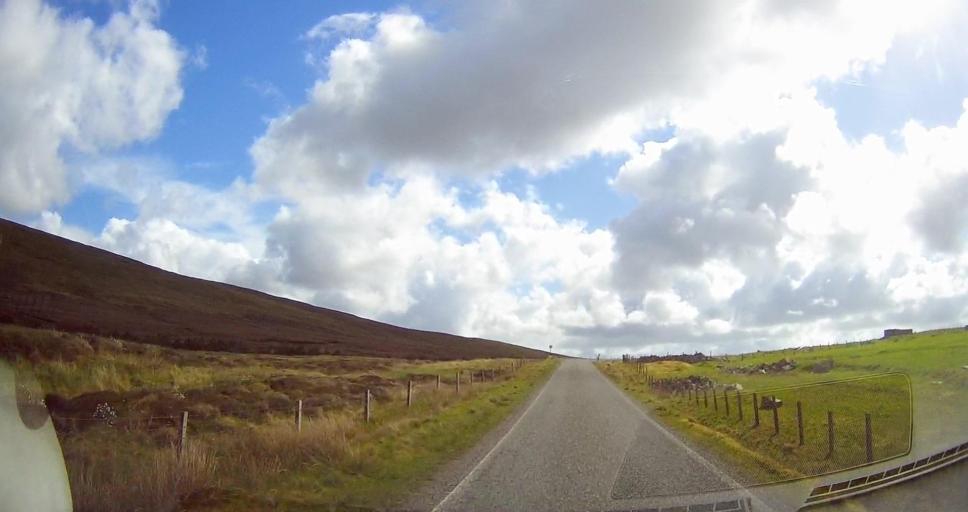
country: GB
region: Scotland
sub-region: Shetland Islands
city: Lerwick
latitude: 60.5090
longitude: -1.3867
